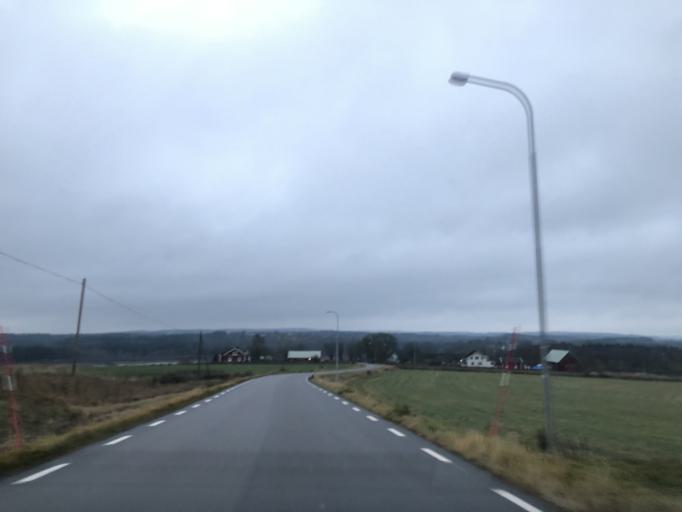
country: SE
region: Vaestra Goetaland
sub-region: Ulricehamns Kommun
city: Ulricehamn
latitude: 57.8436
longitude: 13.2311
